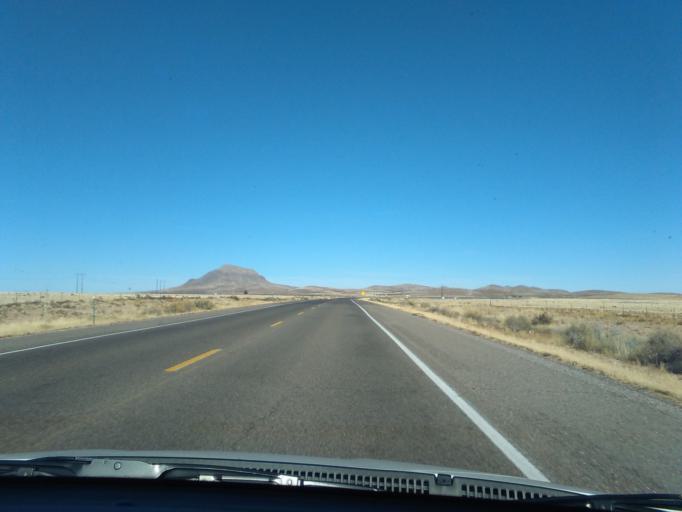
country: US
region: New Mexico
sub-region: Dona Ana County
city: Hatch
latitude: 32.5557
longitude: -107.4737
